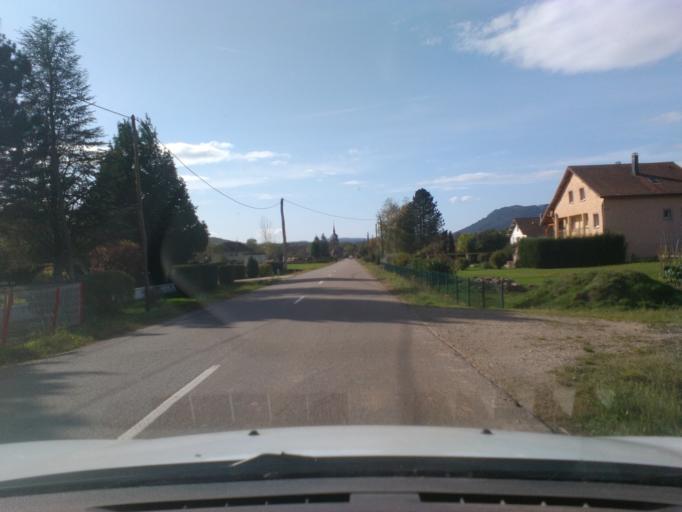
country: FR
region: Lorraine
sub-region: Departement des Vosges
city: Sainte-Marguerite
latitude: 48.2723
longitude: 7.0081
